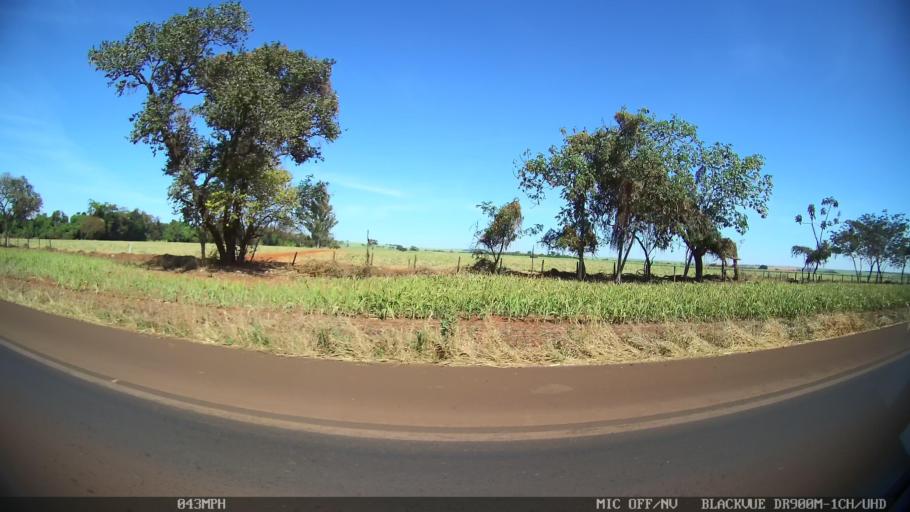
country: BR
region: Sao Paulo
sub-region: Ipua
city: Ipua
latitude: -20.5049
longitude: -47.9338
